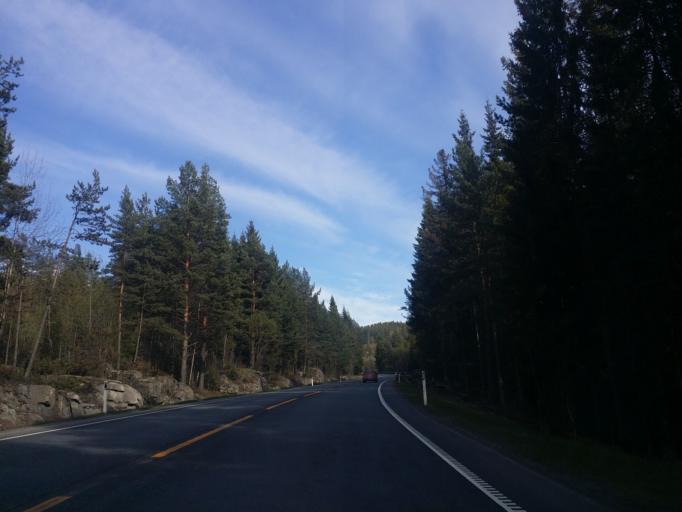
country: NO
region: Telemark
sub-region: Notodden
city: Notodden
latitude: 59.5840
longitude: 9.3107
